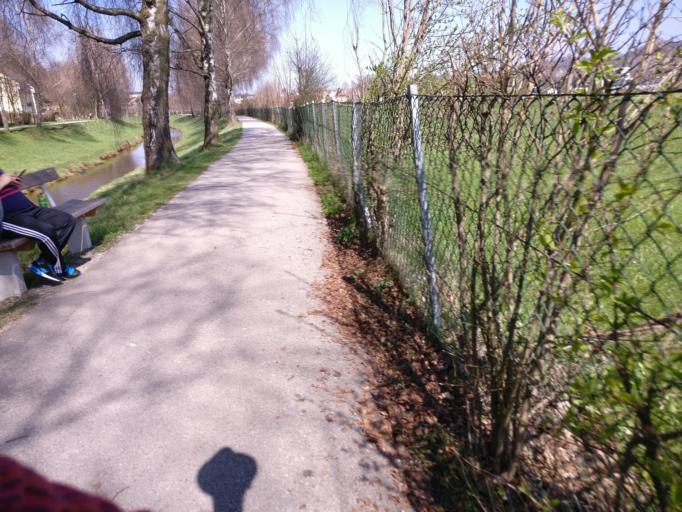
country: AT
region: Salzburg
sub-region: Salzburg Stadt
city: Salzburg
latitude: 47.7872
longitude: 13.0206
